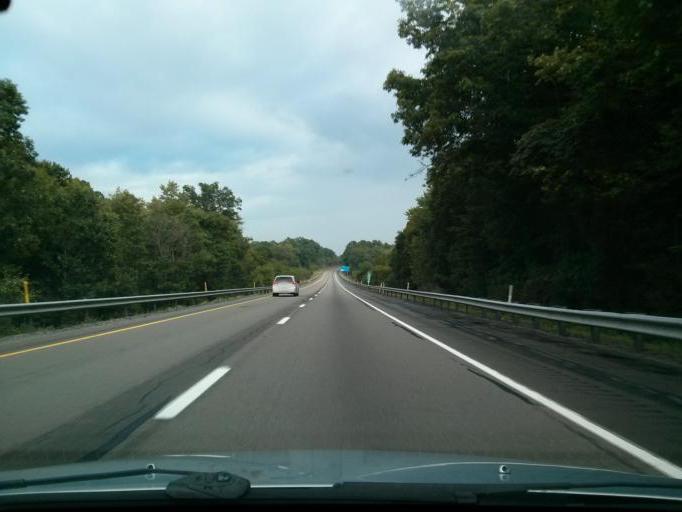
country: US
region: Pennsylvania
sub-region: Jefferson County
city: Brookville
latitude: 41.1781
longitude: -79.1272
